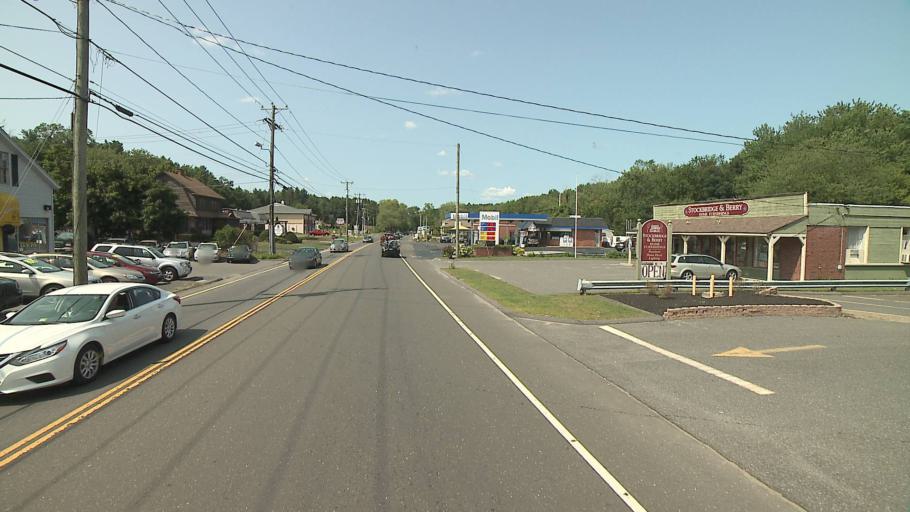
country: US
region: Connecticut
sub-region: Fairfield County
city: Trumbull
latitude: 41.3051
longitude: -73.2549
